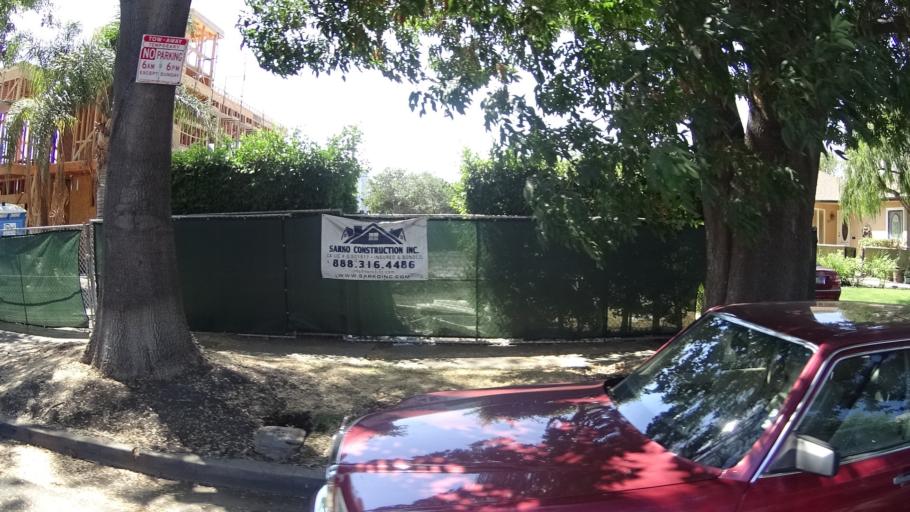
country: US
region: California
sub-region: Los Angeles County
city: West Hollywood
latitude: 34.0769
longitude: -118.3711
